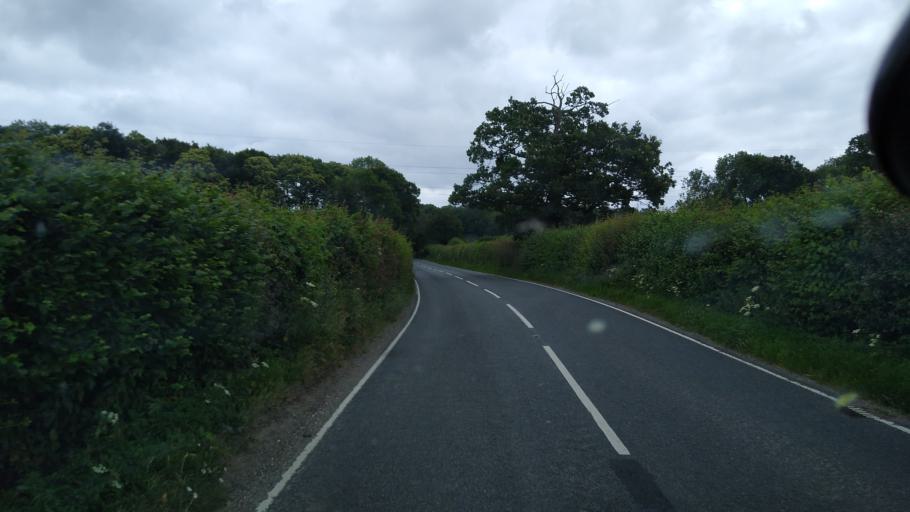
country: GB
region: England
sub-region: Hampshire
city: Alton
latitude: 51.1303
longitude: -0.9617
